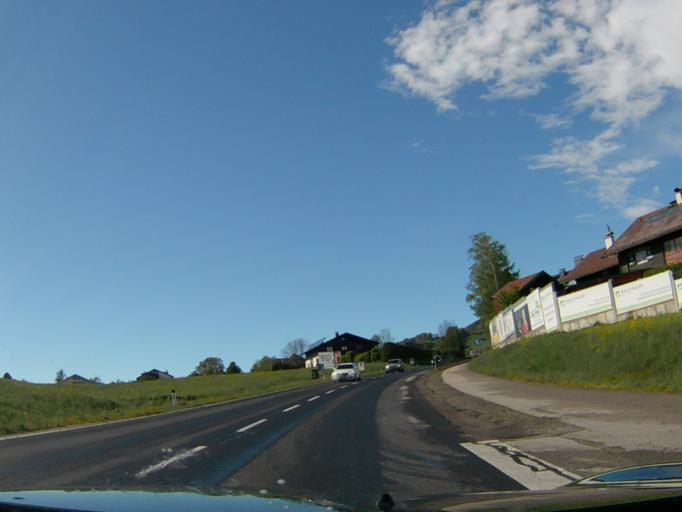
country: AT
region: Upper Austria
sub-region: Politischer Bezirk Vocklabruck
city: Mondsee
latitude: 47.8546
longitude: 13.3430
